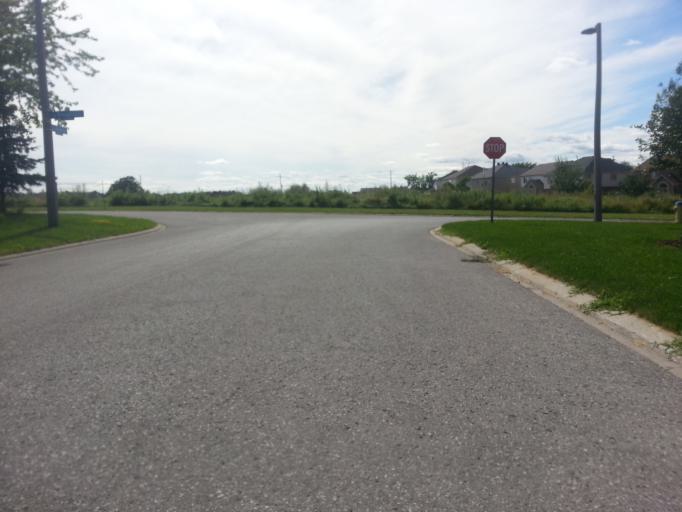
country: CA
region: Ontario
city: Bells Corners
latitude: 45.3252
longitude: -75.9262
